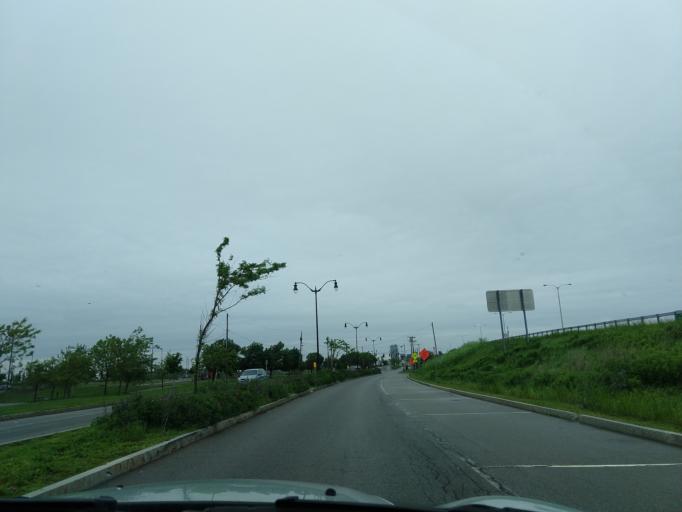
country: US
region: New York
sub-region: Erie County
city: Lackawanna
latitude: 42.8444
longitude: -78.8601
